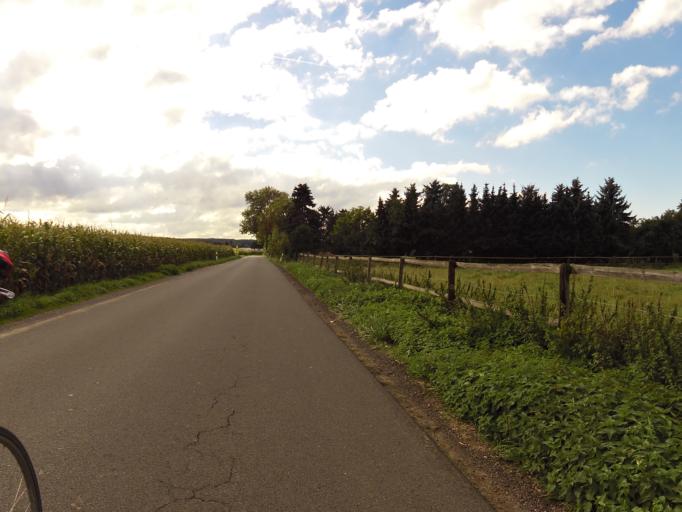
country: DE
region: North Rhine-Westphalia
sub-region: Regierungsbezirk Koln
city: Euskirchen
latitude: 50.6387
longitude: 6.8199
